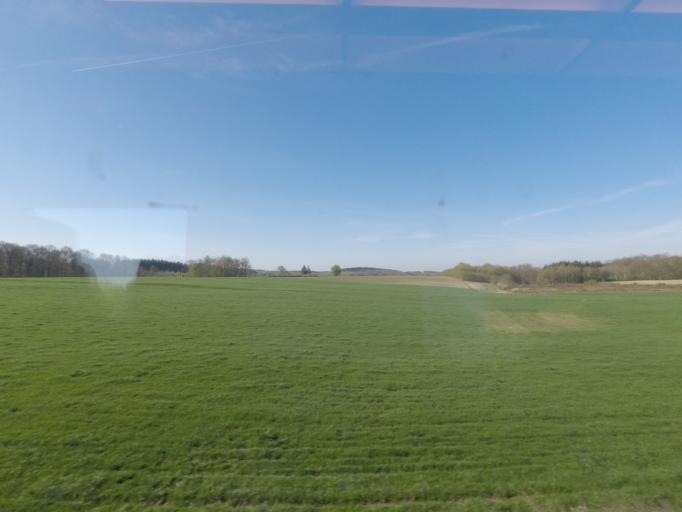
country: BE
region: Wallonia
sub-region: Province de Namur
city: Hamois
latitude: 50.2652
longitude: 5.1746
